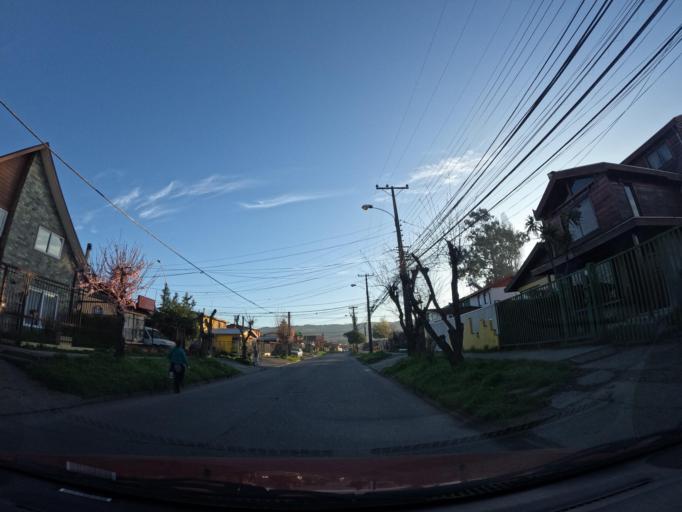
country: CL
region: Biobio
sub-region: Provincia de Concepcion
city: Chiguayante
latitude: -36.9209
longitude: -73.0294
